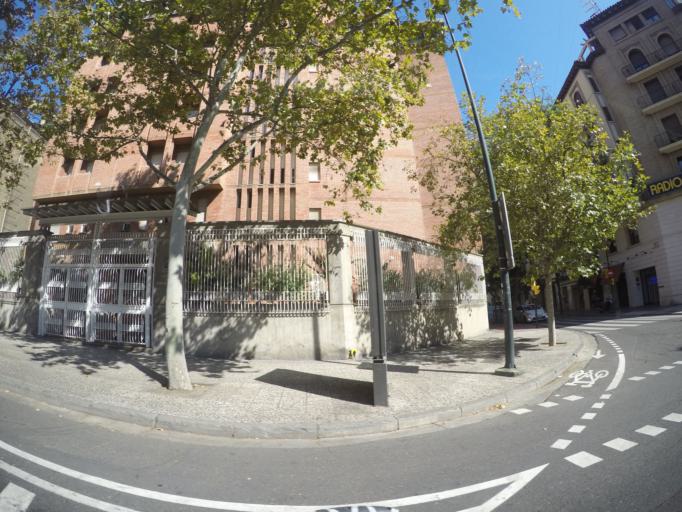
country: ES
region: Aragon
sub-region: Provincia de Zaragoza
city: Zaragoza
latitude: 41.6484
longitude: -0.8820
